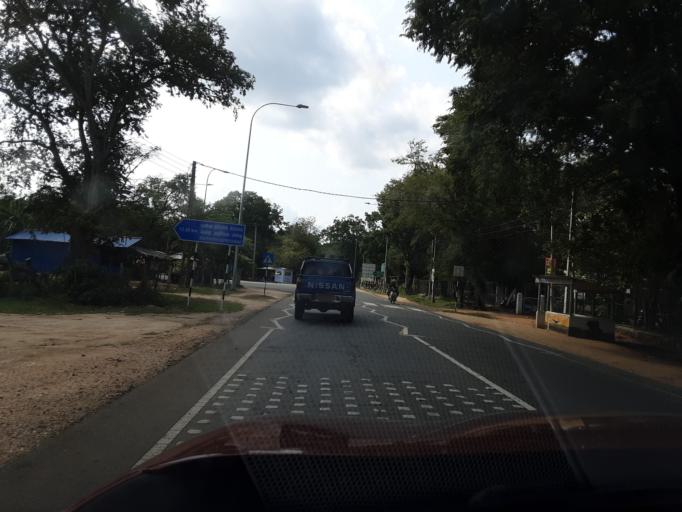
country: LK
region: Uva
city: Haputale
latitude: 6.3607
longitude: 81.1815
